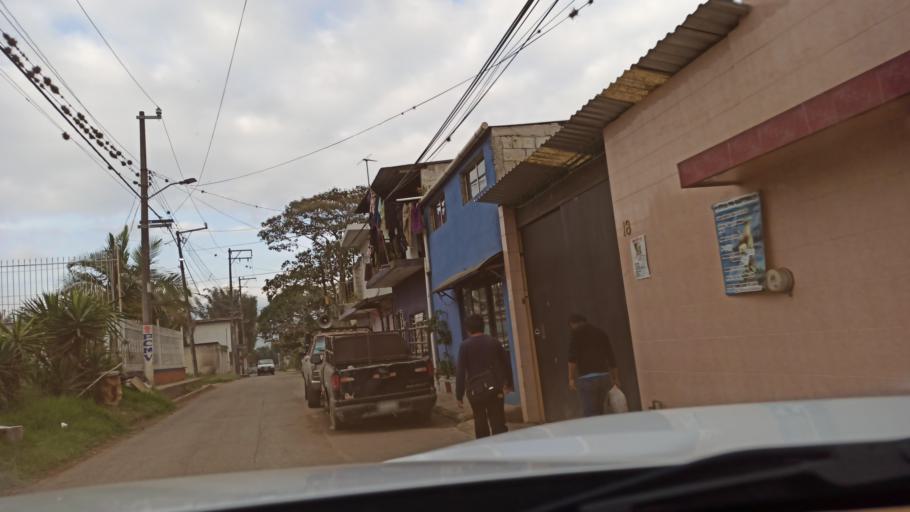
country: MX
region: Veracruz
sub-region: Fortin
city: Monte Salas
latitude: 18.9241
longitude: -97.0107
